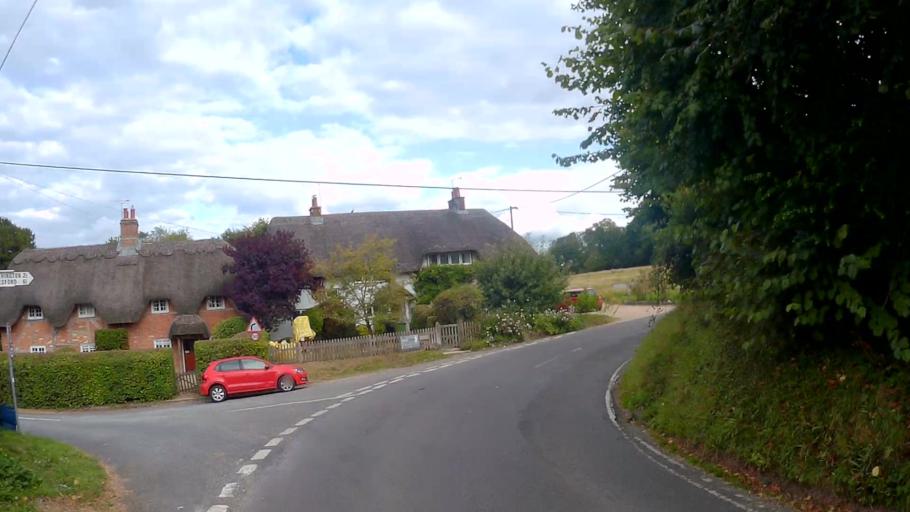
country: GB
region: England
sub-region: Hampshire
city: Overton
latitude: 51.1572
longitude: -1.2271
